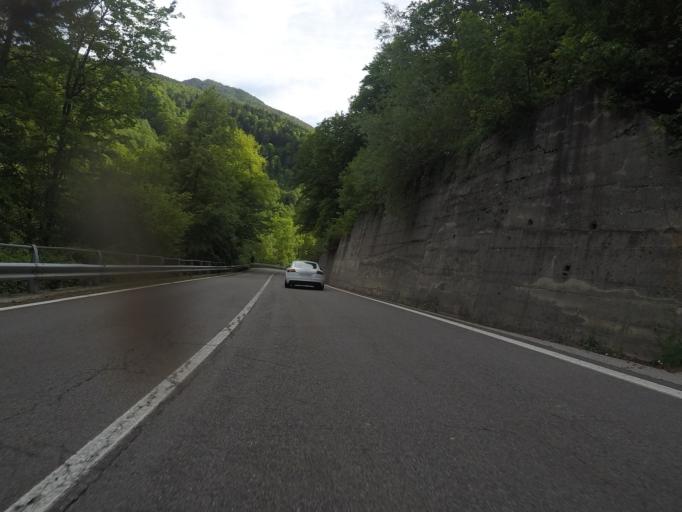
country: IT
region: Piedmont
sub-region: Provincia Verbano-Cusio-Ossola
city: Druogno
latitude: 46.1287
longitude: 8.3943
